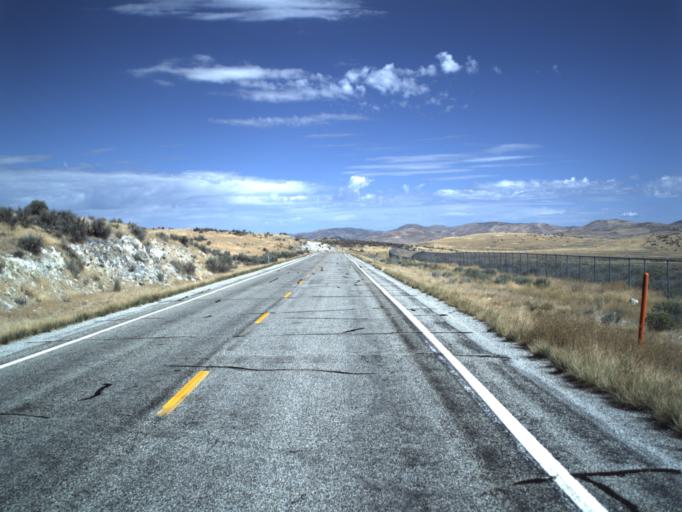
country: US
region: Utah
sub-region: Box Elder County
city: Tremonton
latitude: 41.7177
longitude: -112.4516
